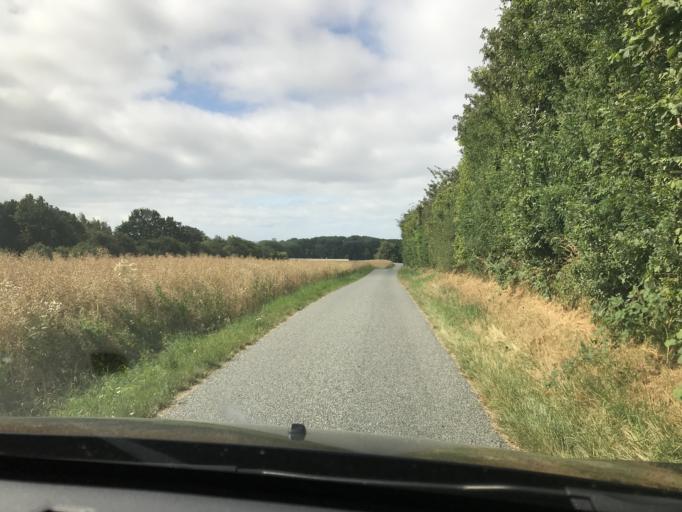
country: DK
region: South Denmark
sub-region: AEro Kommune
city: AEroskobing
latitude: 54.9233
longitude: 10.2883
